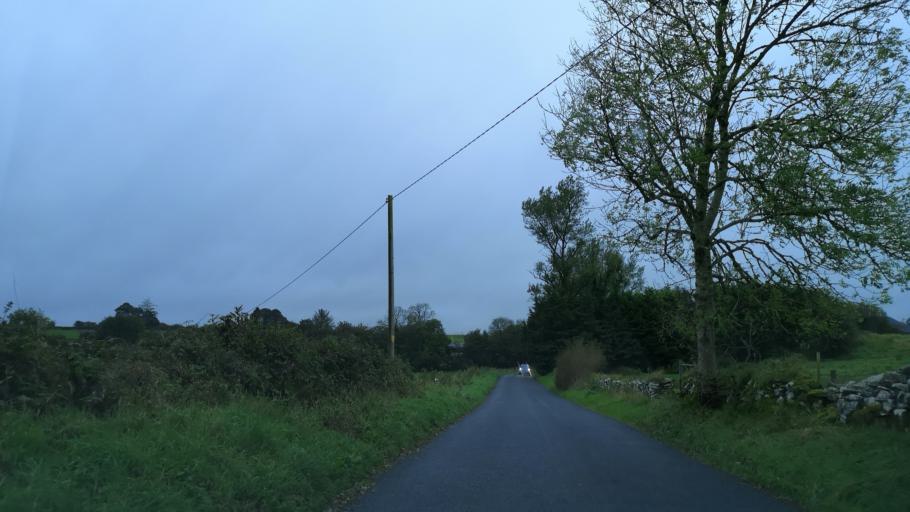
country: IE
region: Connaught
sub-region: Roscommon
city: Ballaghaderreen
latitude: 53.8973
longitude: -8.5992
